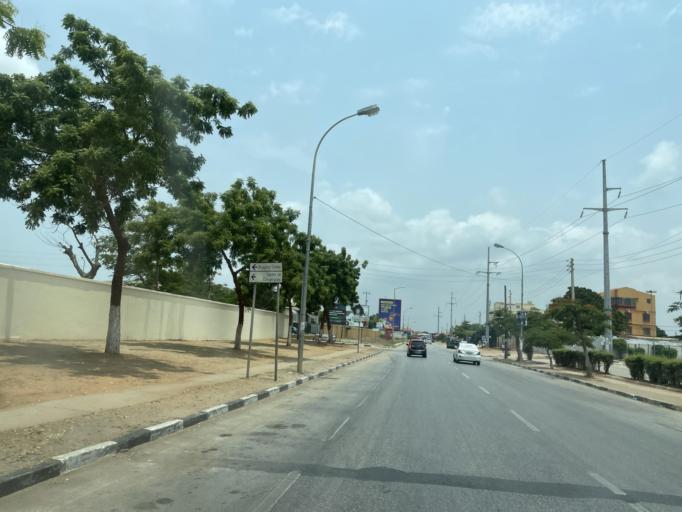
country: AO
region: Luanda
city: Luanda
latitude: -8.9157
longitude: 13.1985
